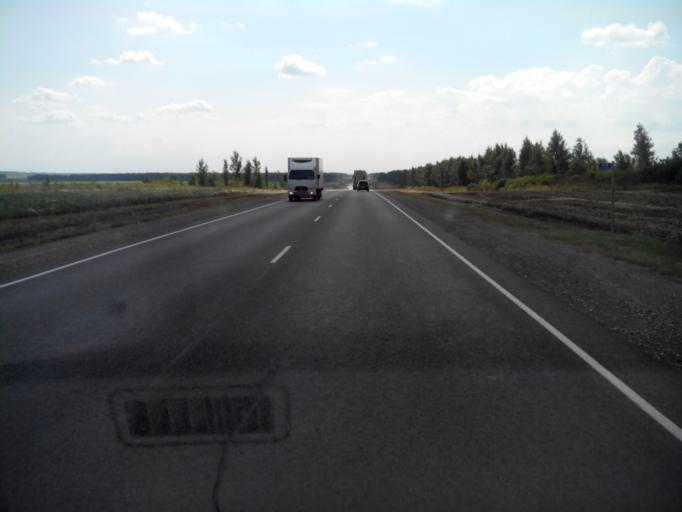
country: RU
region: Penza
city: Kondol'
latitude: 52.7090
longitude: 45.1111
